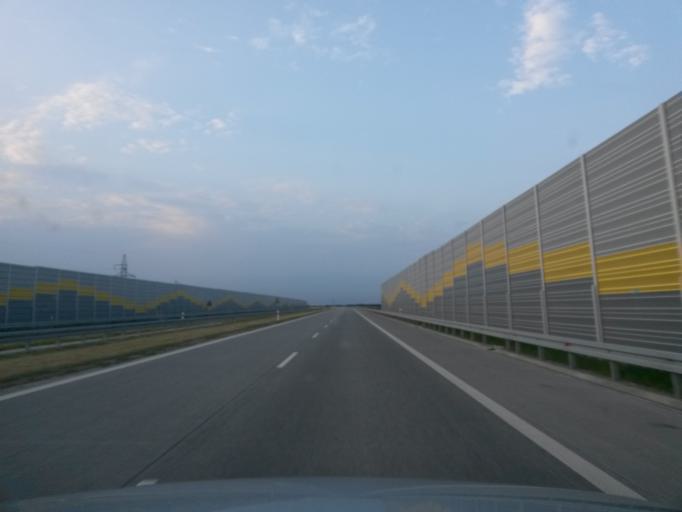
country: PL
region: Lodz Voivodeship
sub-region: Powiat sieradzki
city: Brzeznio
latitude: 51.4665
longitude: 18.6597
